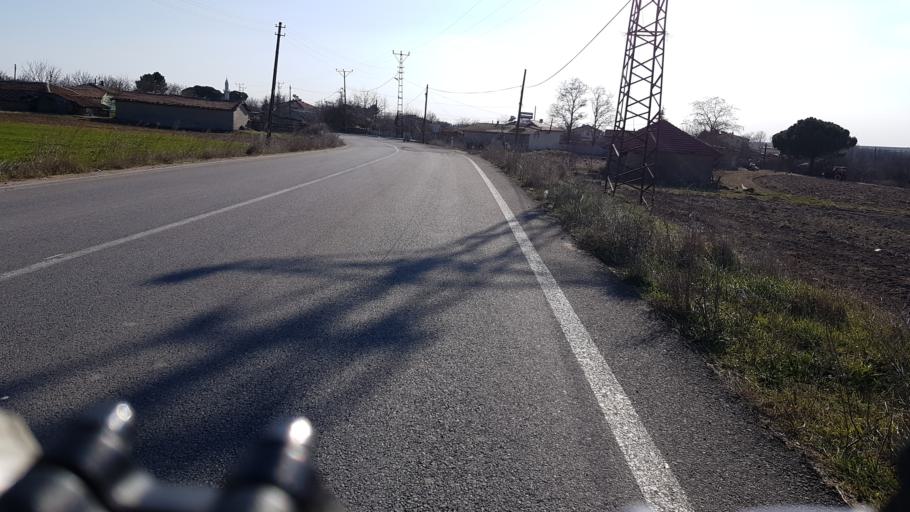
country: TR
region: Tekirdag
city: Velimese
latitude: 41.3475
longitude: 27.8368
